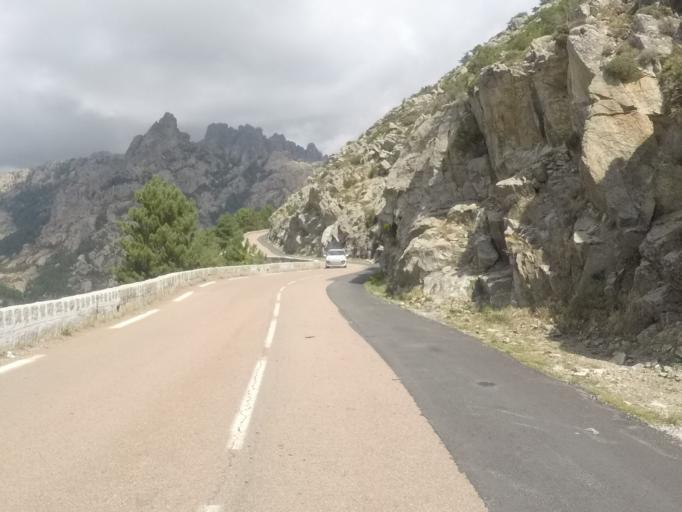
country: FR
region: Corsica
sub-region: Departement de la Corse-du-Sud
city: Zonza
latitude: 41.7826
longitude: 9.2192
